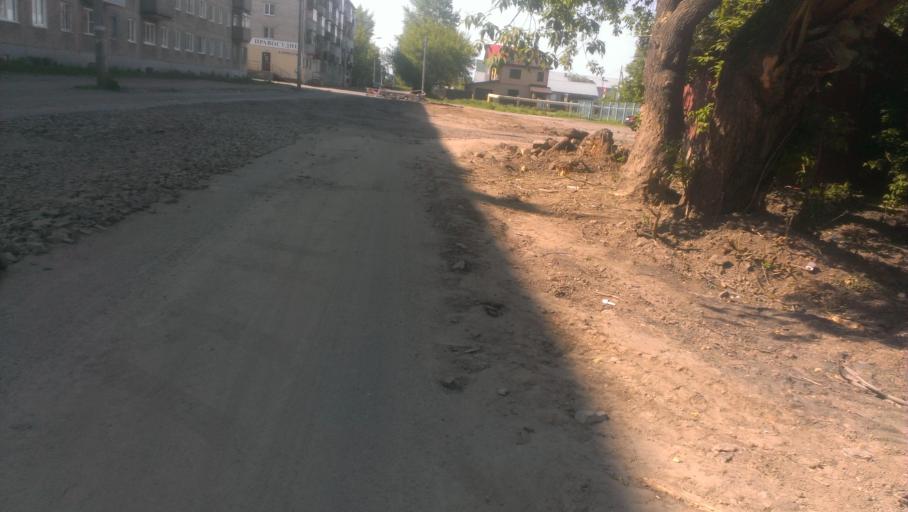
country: RU
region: Altai Krai
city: Novoaltaysk
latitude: 53.3956
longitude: 83.9364
